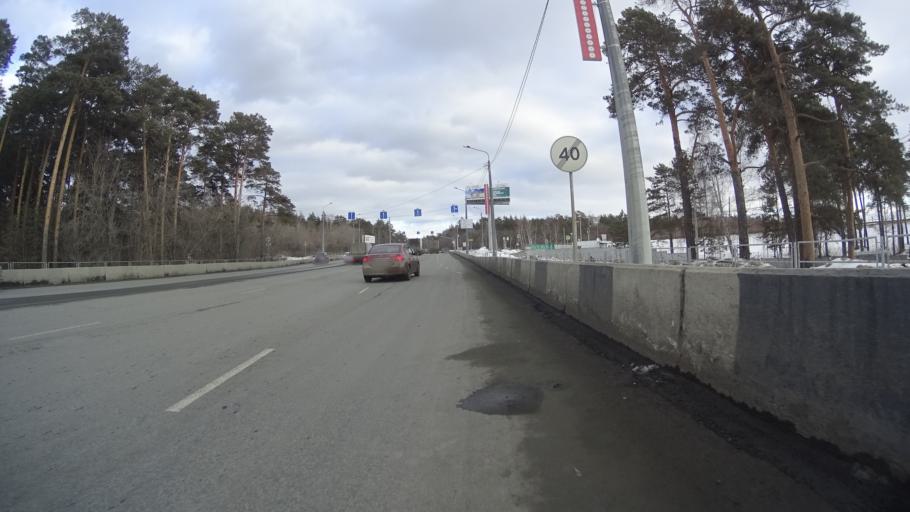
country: RU
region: Chelyabinsk
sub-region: Gorod Chelyabinsk
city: Chelyabinsk
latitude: 55.1476
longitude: 61.3274
